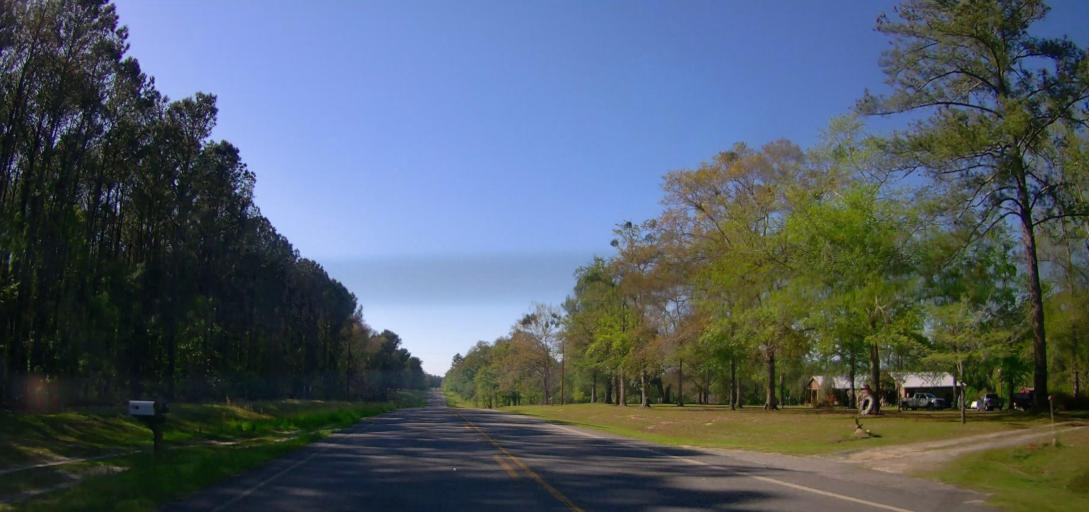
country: US
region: Georgia
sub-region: Wilcox County
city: Rochelle
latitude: 32.0052
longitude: -83.4853
